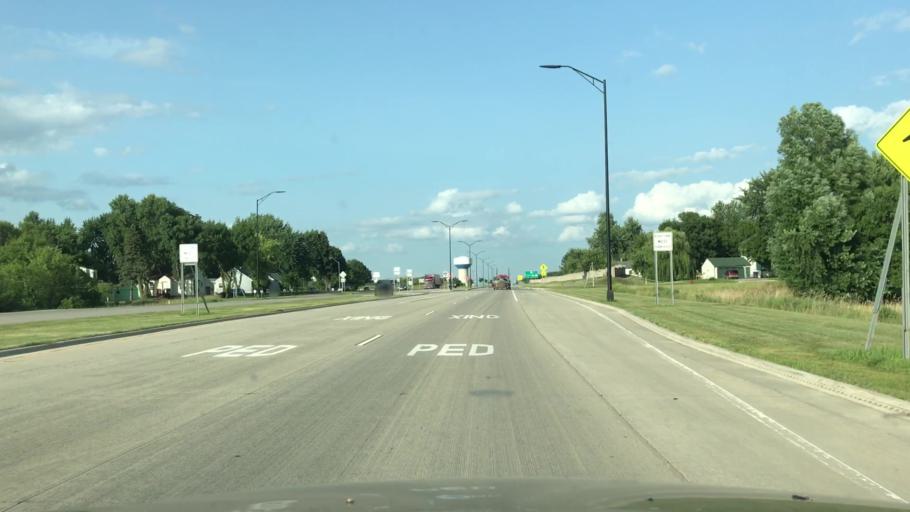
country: US
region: Minnesota
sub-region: Nobles County
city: Worthington
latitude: 43.6170
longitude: -95.5873
